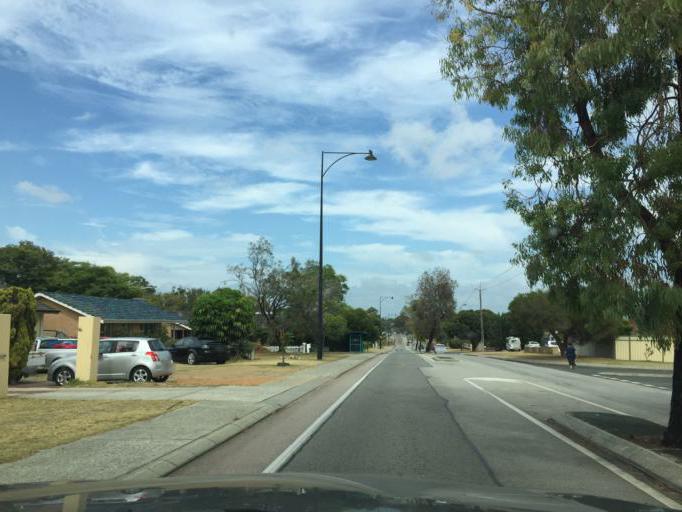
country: AU
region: Western Australia
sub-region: Melville
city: Kardinya
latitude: -32.0747
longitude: 115.8089
